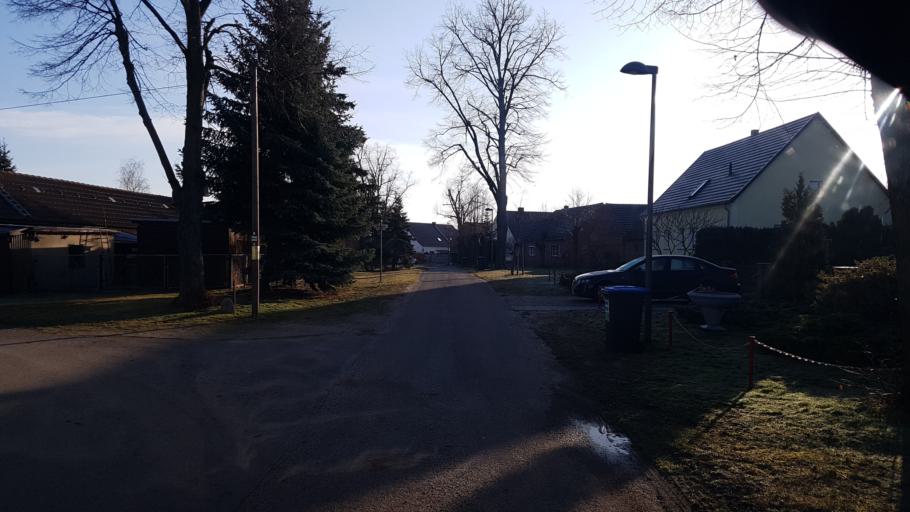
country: DE
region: Brandenburg
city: Calau
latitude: 51.7348
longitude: 13.9009
